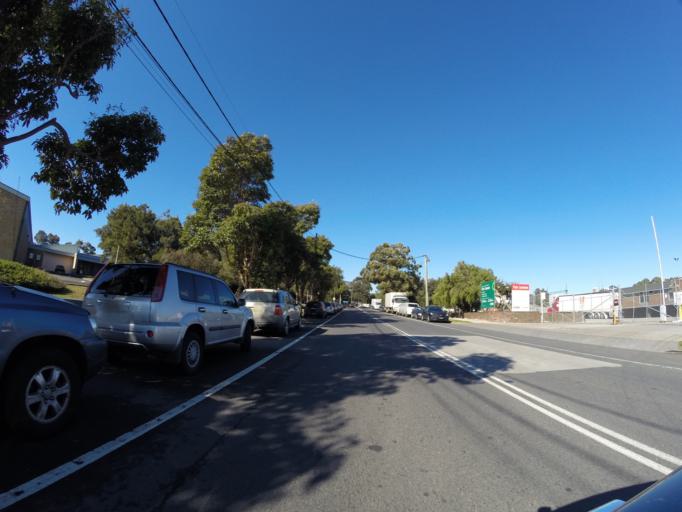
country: AU
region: New South Wales
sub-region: Canada Bay
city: Concord West
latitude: -33.8521
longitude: 151.0616
